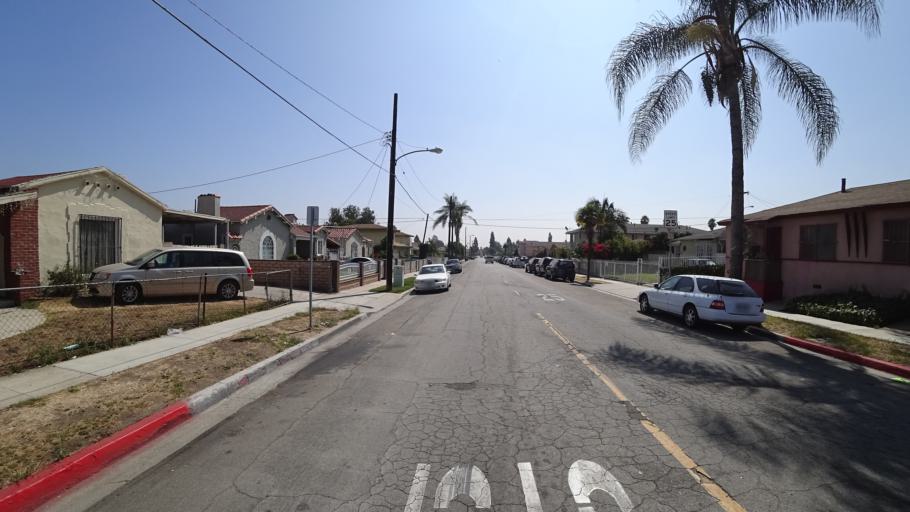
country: US
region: California
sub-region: Los Angeles County
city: Westmont
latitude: 33.9413
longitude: -118.2961
